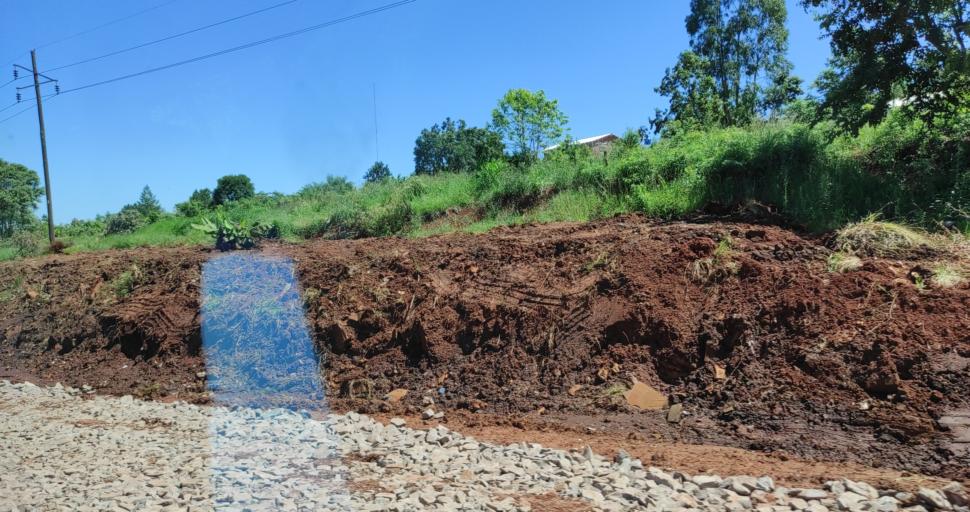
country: AR
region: Misiones
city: El Soberbio
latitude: -27.2867
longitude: -54.2213
